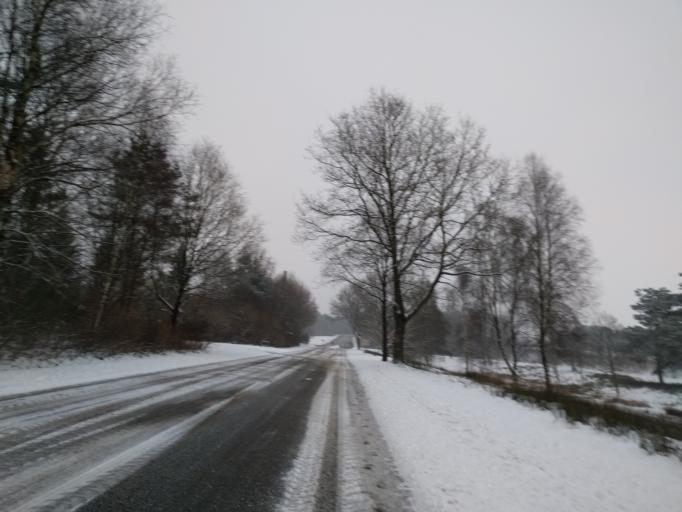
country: DK
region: Central Jutland
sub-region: Viborg Kommune
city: Viborg
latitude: 56.4249
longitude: 9.3966
